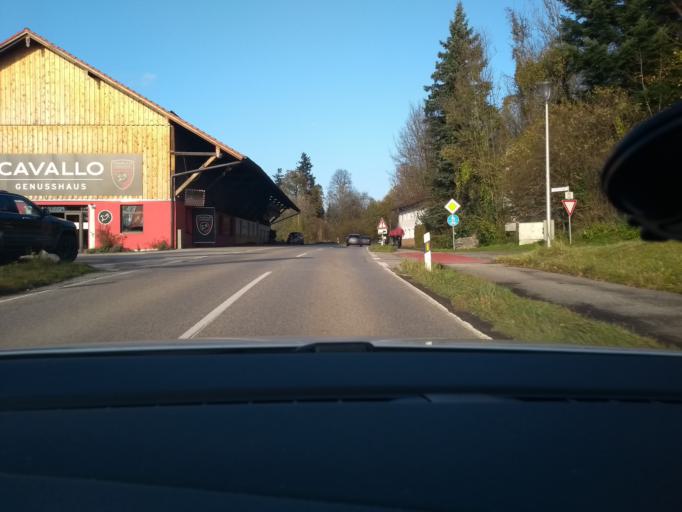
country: DE
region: Bavaria
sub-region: Upper Bavaria
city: Stephanskirchen
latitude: 47.8326
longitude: 12.1553
